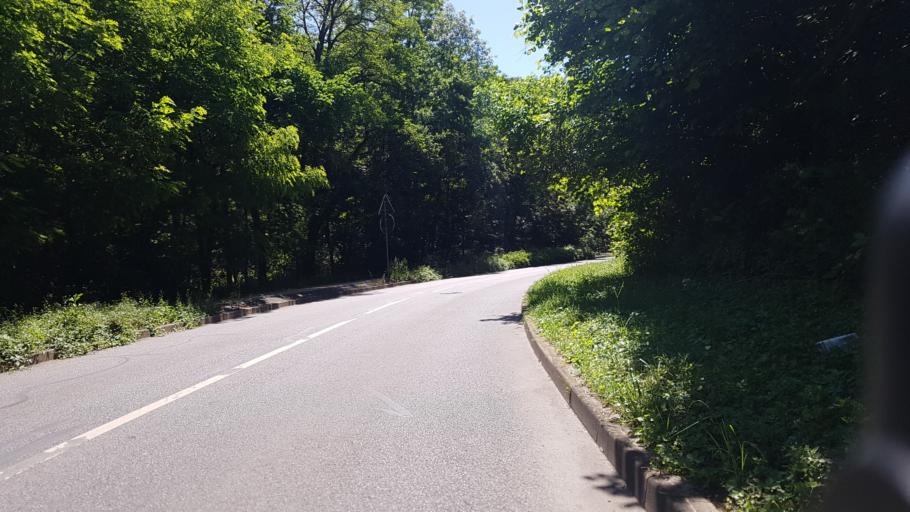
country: FR
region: Rhone-Alpes
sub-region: Departement du Rhone
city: Sathonay-Village
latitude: 45.8295
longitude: 4.8779
